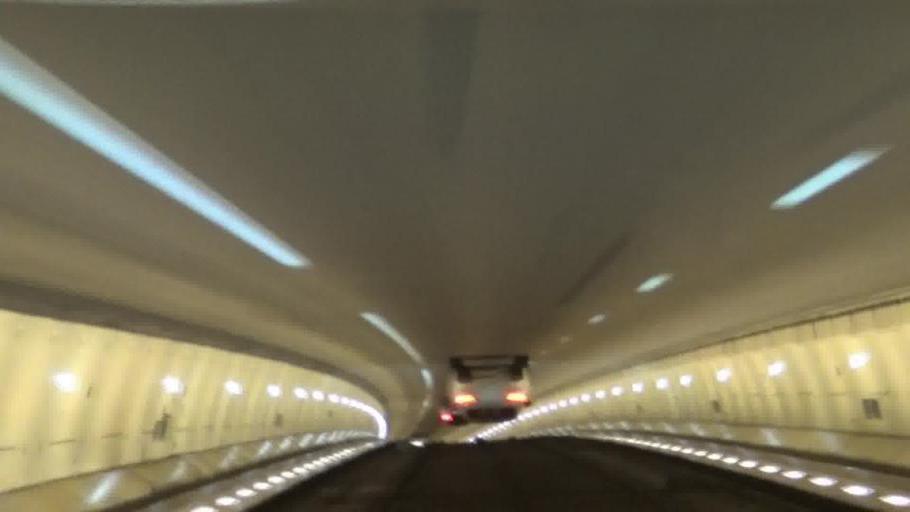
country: FR
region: Ile-de-France
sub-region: Departement des Yvelines
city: Viroflay
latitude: 48.8162
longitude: 2.1573
